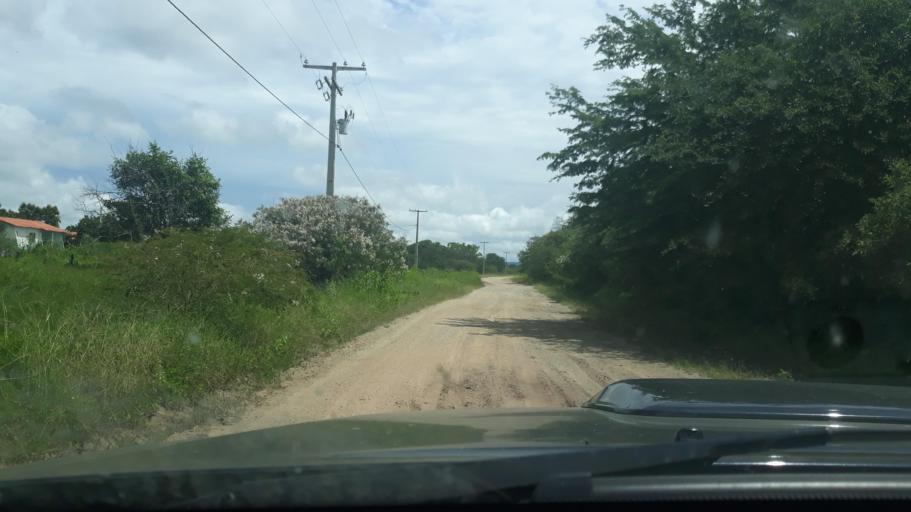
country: BR
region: Bahia
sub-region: Riacho De Santana
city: Riacho de Santana
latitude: -13.8753
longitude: -43.0205
